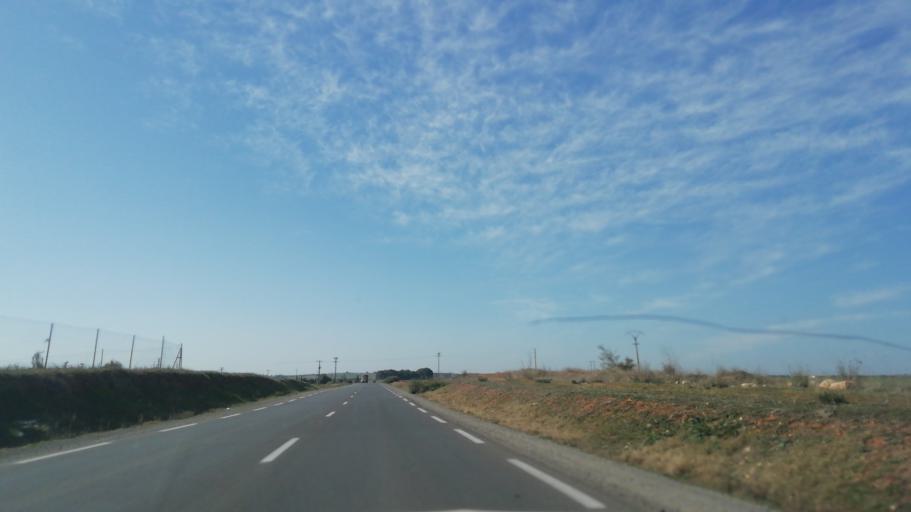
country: DZ
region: Tlemcen
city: Ouled Mimoun
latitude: 35.0358
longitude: -0.8579
